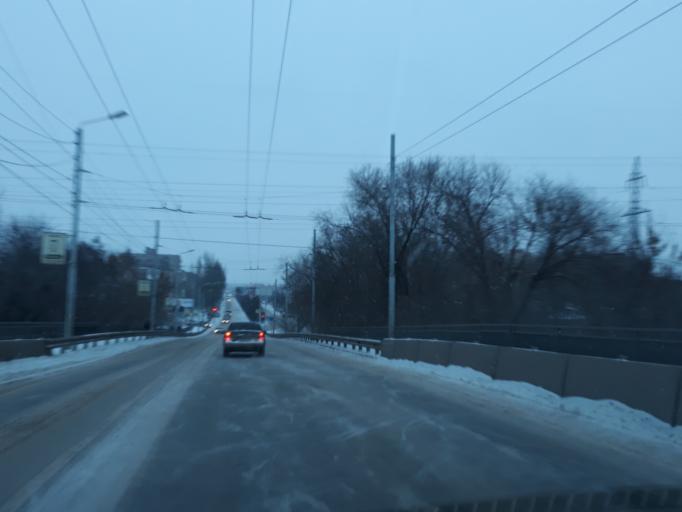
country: RU
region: Rostov
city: Taganrog
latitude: 47.2658
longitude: 38.9247
